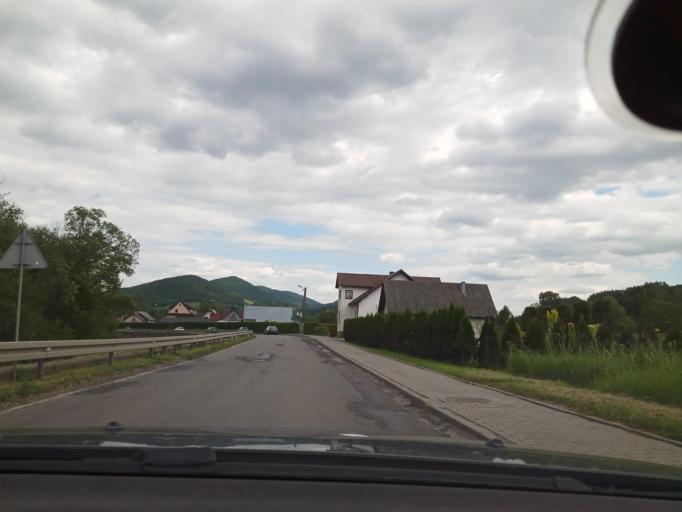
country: PL
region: Lesser Poland Voivodeship
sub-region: Powiat limanowski
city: Tymbark
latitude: 49.7400
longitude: 20.3749
